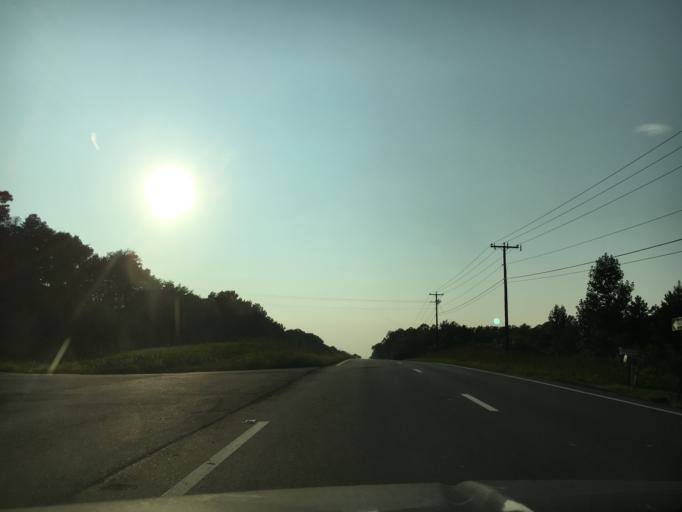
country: US
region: Virginia
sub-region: Appomattox County
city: Appomattox
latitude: 37.2808
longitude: -78.7029
